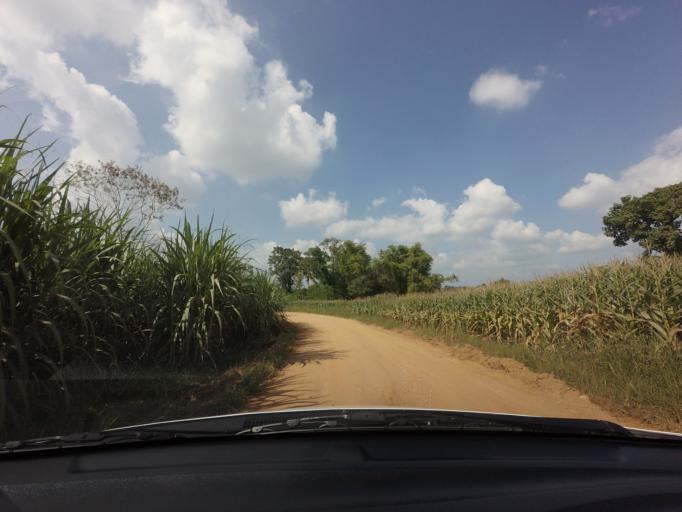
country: TH
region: Nakhon Ratchasima
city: Wang Nam Khiao
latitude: 14.4984
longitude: 101.6310
